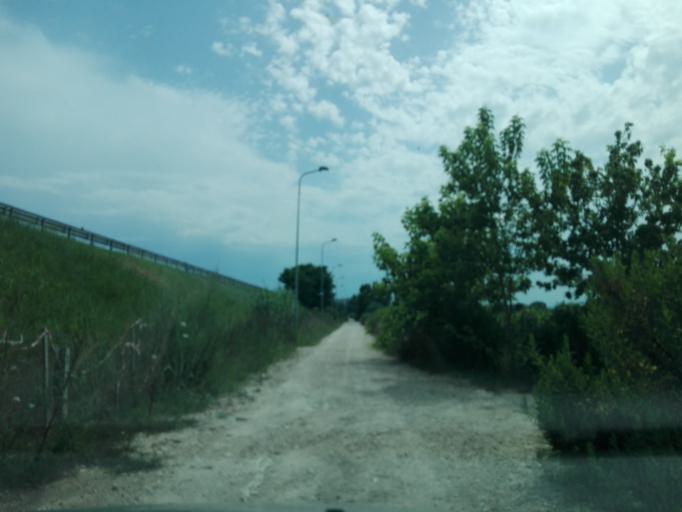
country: IT
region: Abruzzo
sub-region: Provincia di Pescara
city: Cappelle sul Tavo
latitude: 42.4933
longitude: 14.1132
